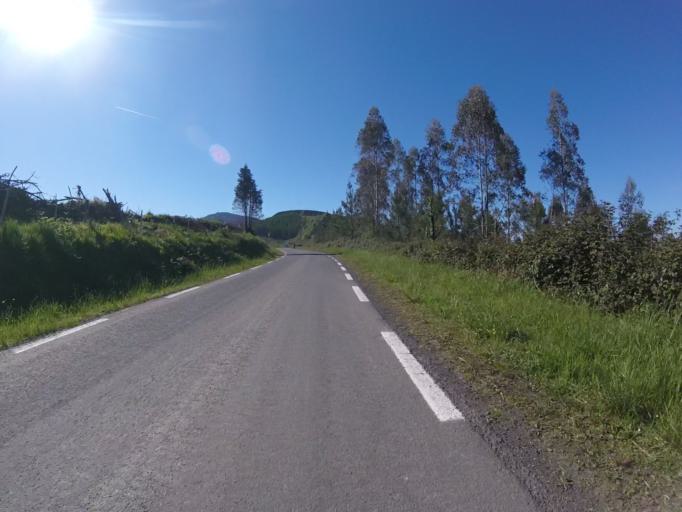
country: ES
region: Basque Country
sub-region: Provincia de Guipuzcoa
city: Errezil
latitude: 43.2066
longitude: -2.1988
